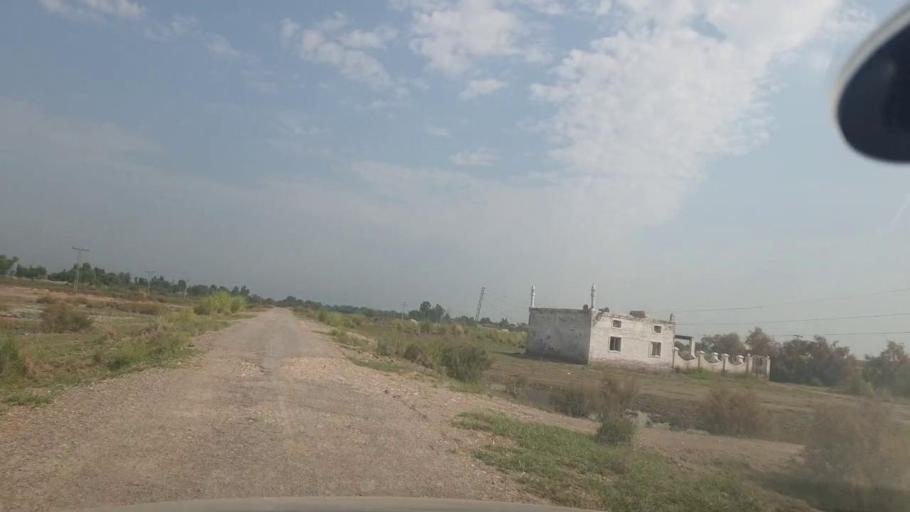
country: PK
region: Balochistan
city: Mehrabpur
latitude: 28.0555
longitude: 68.1239
